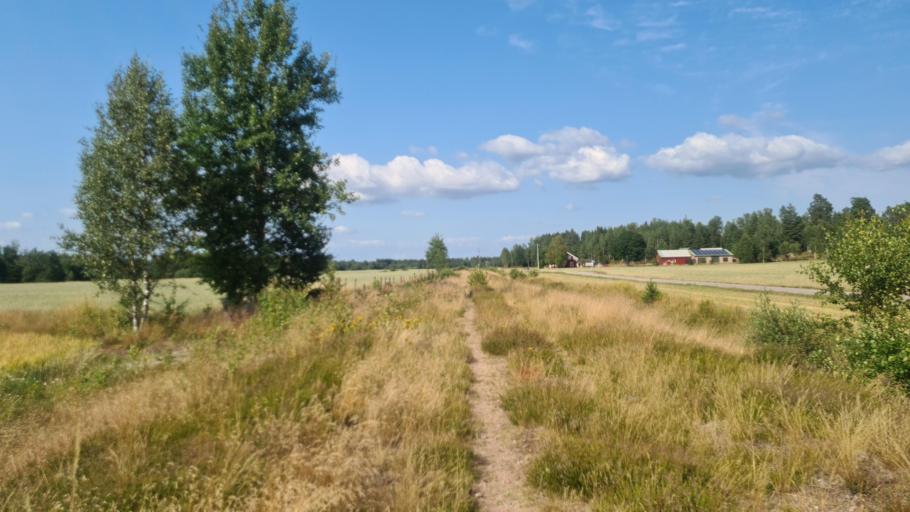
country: SE
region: Kronoberg
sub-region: Ljungby Kommun
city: Ljungby
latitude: 56.7503
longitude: 13.8826
